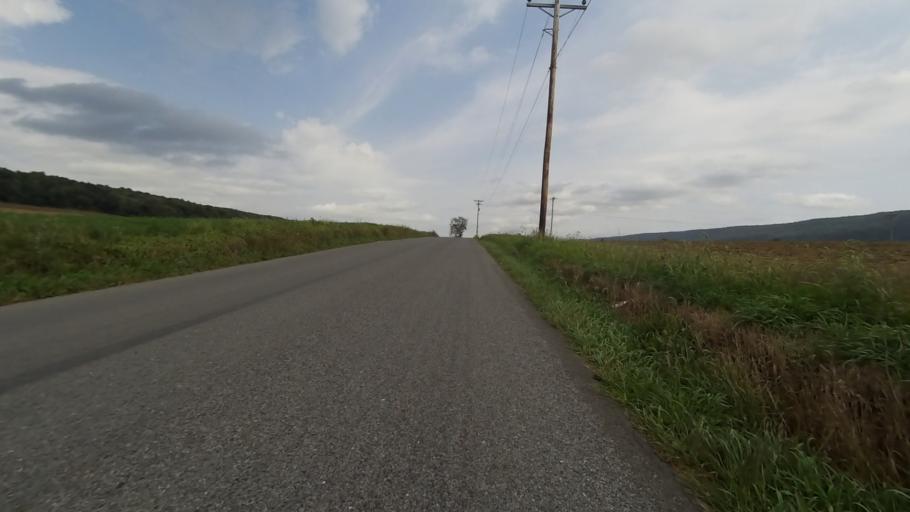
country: US
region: Pennsylvania
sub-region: Blair County
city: Williamsburg
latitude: 40.4809
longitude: -78.1893
